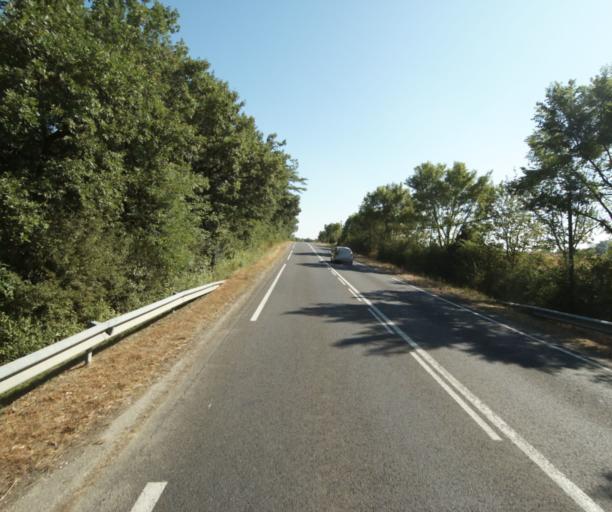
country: FR
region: Midi-Pyrenees
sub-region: Departement de la Haute-Garonne
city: Revel
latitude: 43.4785
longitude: 2.0184
